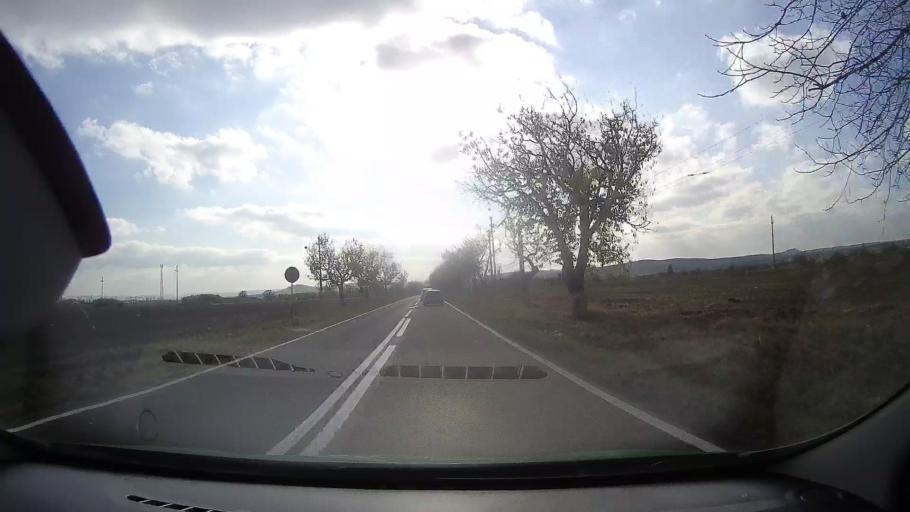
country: RO
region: Tulcea
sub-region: Comuna Nalbant
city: Nalbant
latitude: 45.0555
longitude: 28.6194
